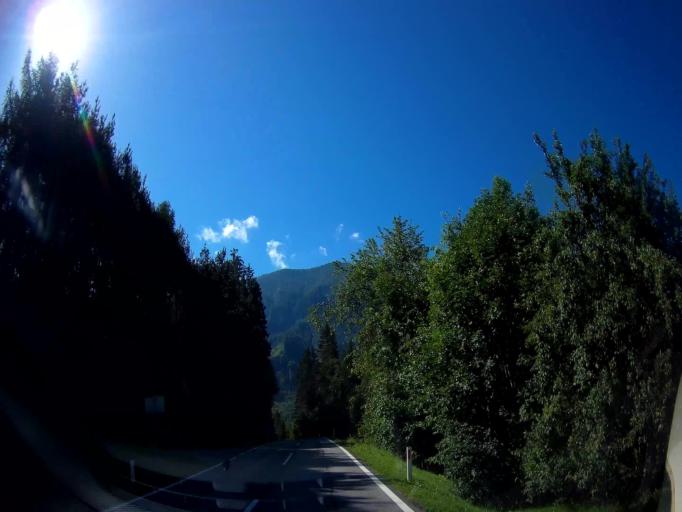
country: AT
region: Carinthia
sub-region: Politischer Bezirk Volkermarkt
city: Gallizien
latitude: 46.5451
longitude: 14.4713
